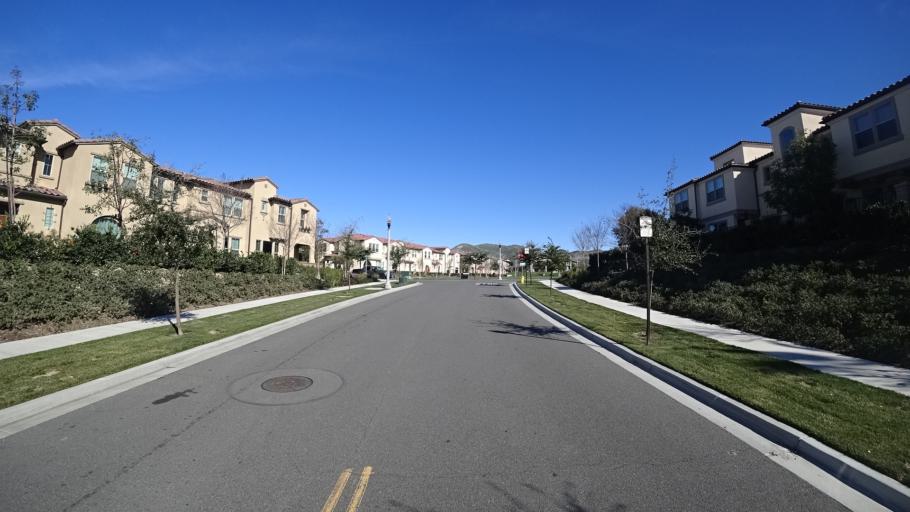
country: US
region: California
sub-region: Orange County
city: Foothill Ranch
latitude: 33.6754
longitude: -117.6782
